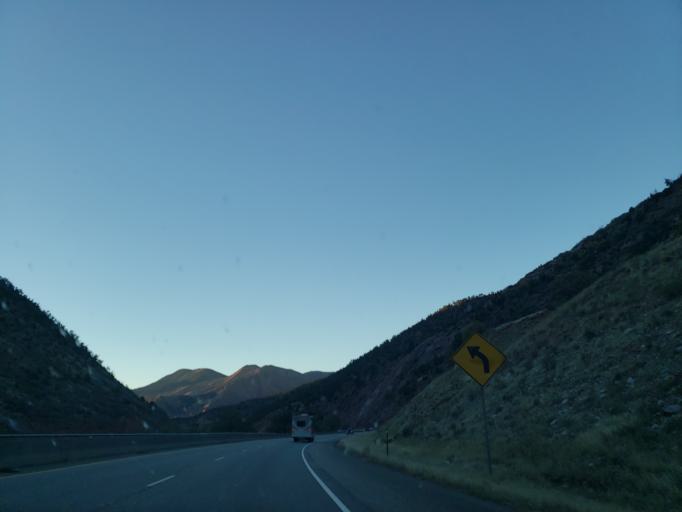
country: US
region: Colorado
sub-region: Garfield County
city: Glenwood Springs
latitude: 39.5675
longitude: -107.4256
